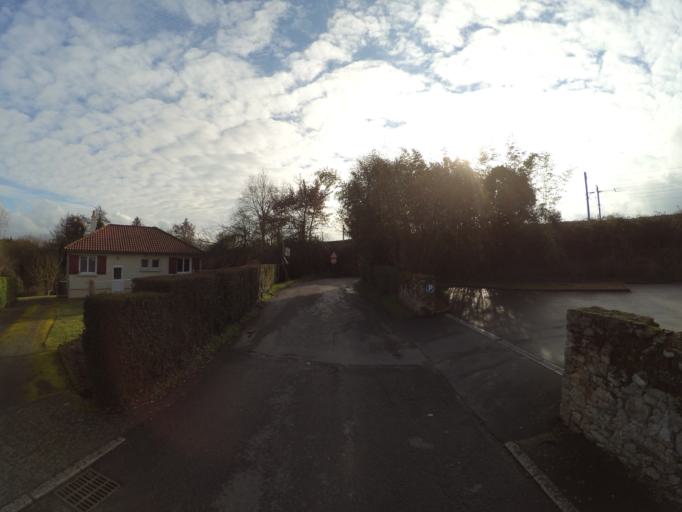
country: FR
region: Pays de la Loire
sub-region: Departement de la Loire-Atlantique
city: Clisson
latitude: 47.0791
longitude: -1.2769
